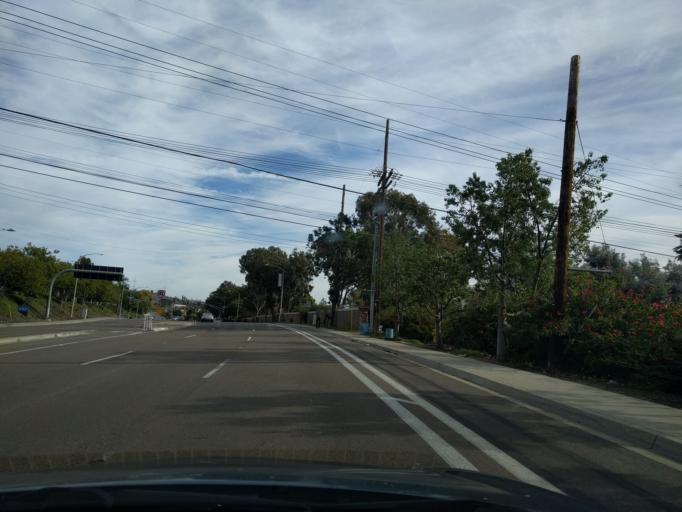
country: US
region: California
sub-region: San Diego County
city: San Diego
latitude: 32.7781
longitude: -117.1359
